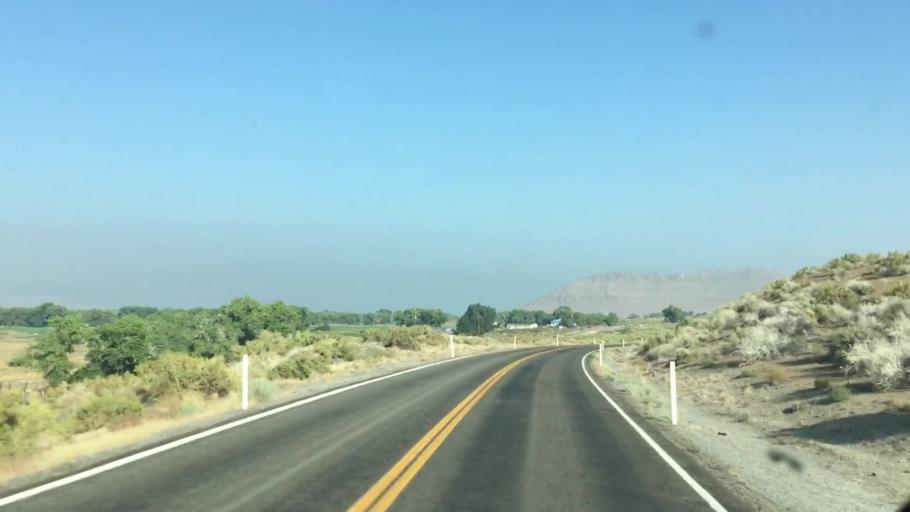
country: US
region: Nevada
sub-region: Lyon County
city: Fernley
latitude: 39.8439
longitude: -119.3651
